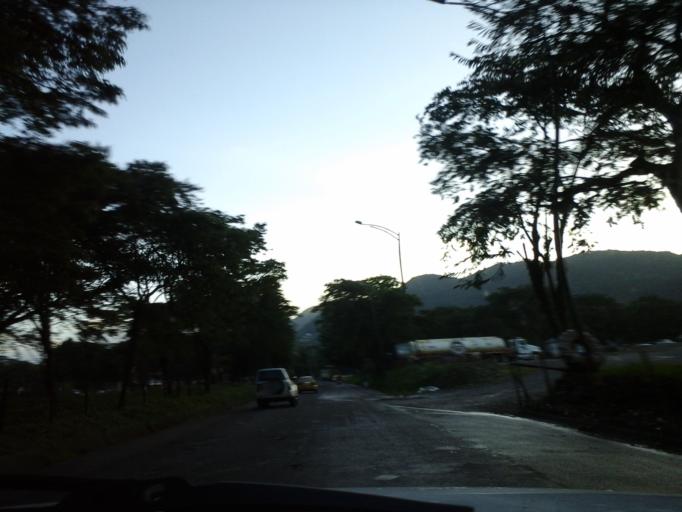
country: CO
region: Meta
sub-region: Villavicencio
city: Villavicencio
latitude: 4.1229
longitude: -73.6435
